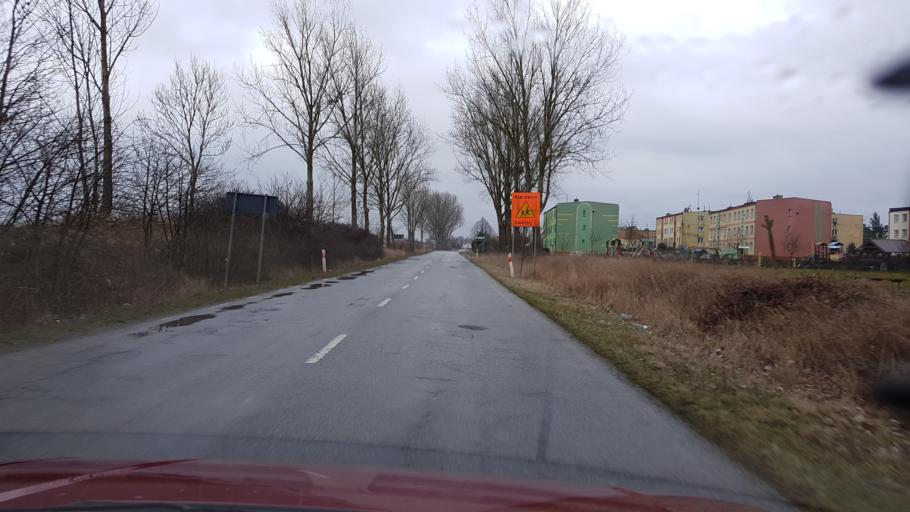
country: PL
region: West Pomeranian Voivodeship
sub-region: Powiat gryfinski
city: Gryfino
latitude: 53.2667
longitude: 14.6149
